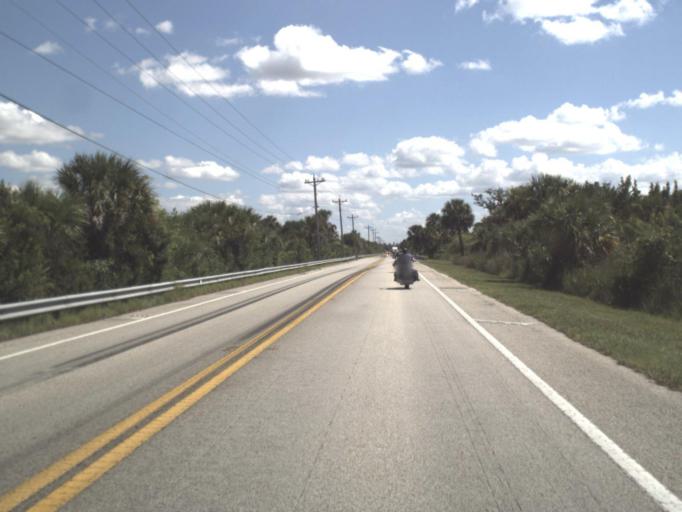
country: US
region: Florida
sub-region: Collier County
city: Marco
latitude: 25.9502
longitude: -81.4820
